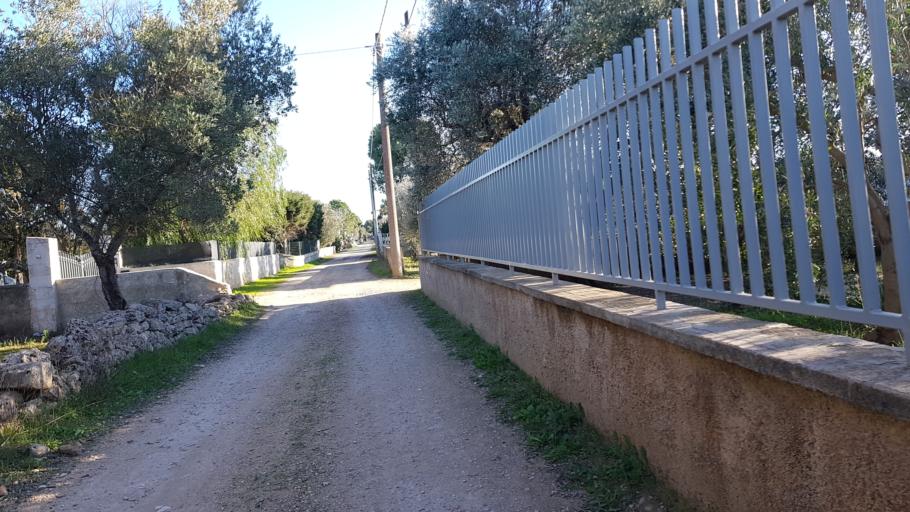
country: IT
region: Apulia
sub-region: Provincia di Lecce
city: Nardo
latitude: 40.1603
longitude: 17.9702
